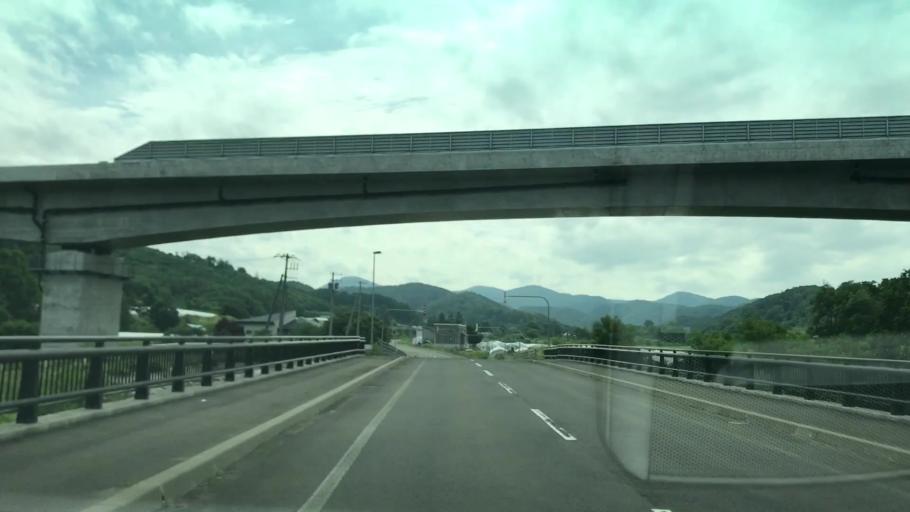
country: JP
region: Hokkaido
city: Yoichi
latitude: 43.1866
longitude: 140.8418
